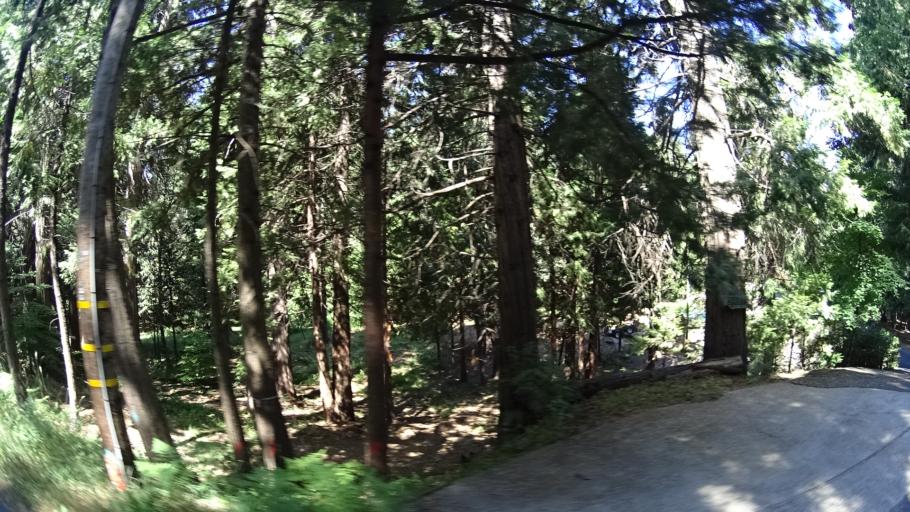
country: US
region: California
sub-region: Calaveras County
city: Arnold
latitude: 38.2393
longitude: -120.3760
